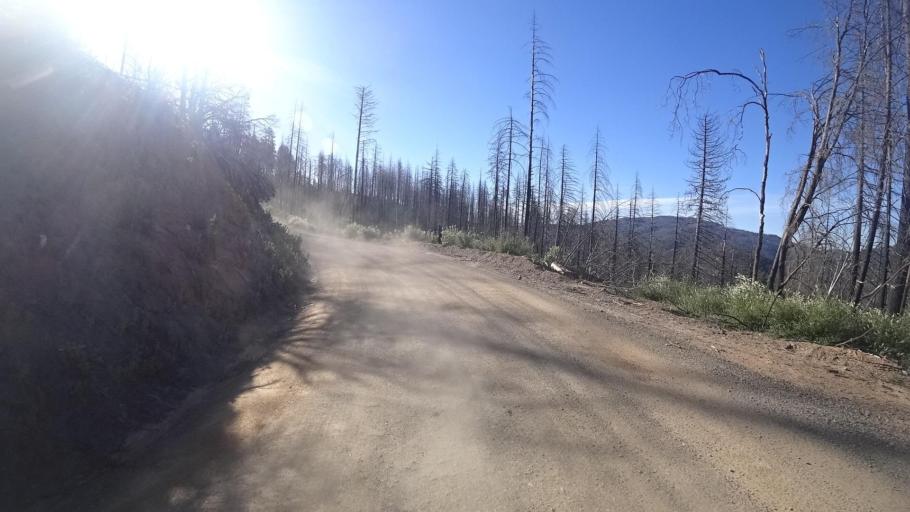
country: US
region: California
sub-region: Lake County
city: Upper Lake
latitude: 39.3598
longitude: -122.9938
